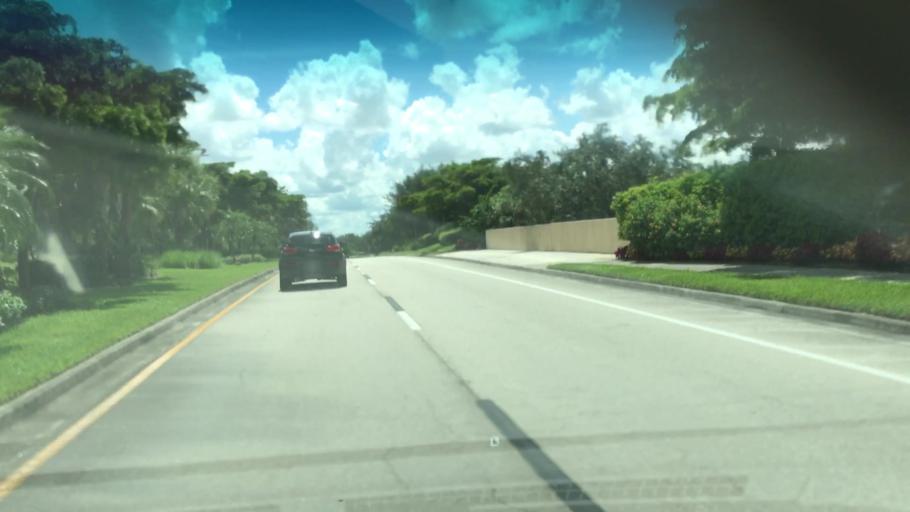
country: US
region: Florida
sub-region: Lee County
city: Estero
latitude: 26.4132
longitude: -81.7859
